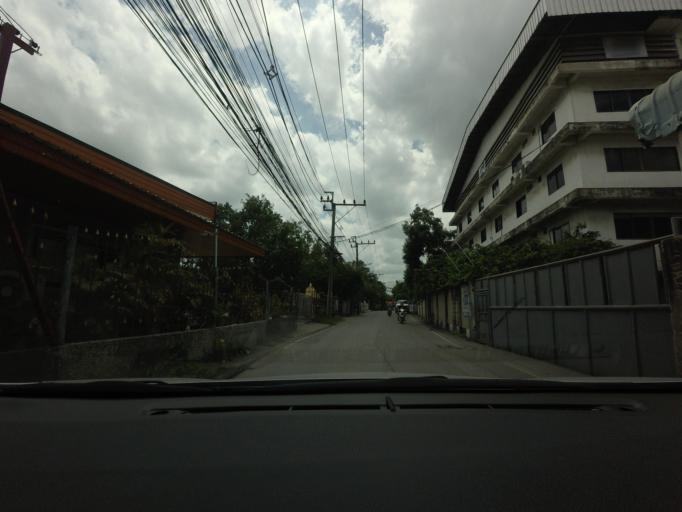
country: TH
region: Samut Prakan
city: Phra Samut Chedi
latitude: 13.6285
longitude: 100.5550
